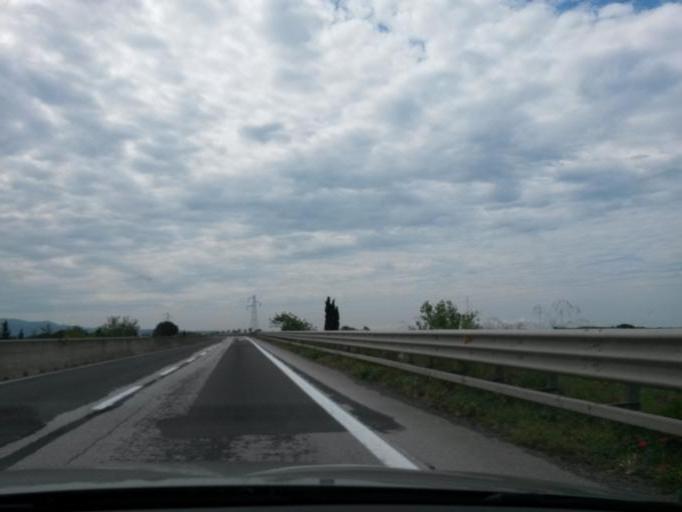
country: IT
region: Tuscany
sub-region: Provincia di Livorno
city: La California
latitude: 43.2371
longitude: 10.5559
